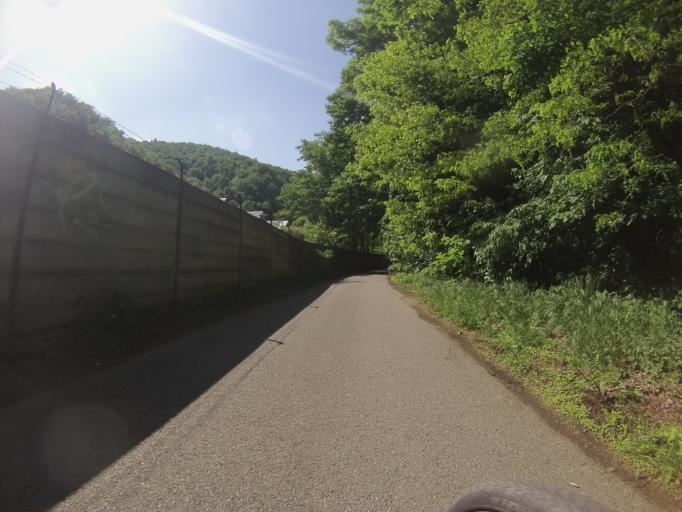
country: CZ
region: South Moravian
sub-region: Okres Blansko
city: Adamov
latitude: 49.3044
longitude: 16.6446
